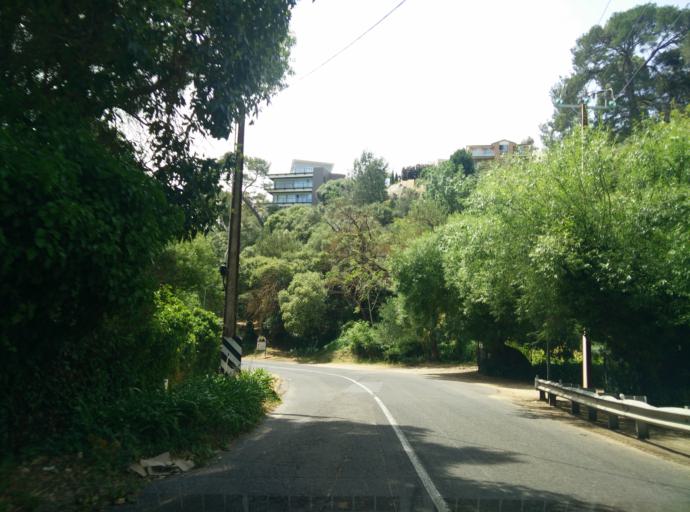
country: AU
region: South Australia
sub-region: Burnside
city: Beaumont
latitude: -34.9461
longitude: 138.6662
